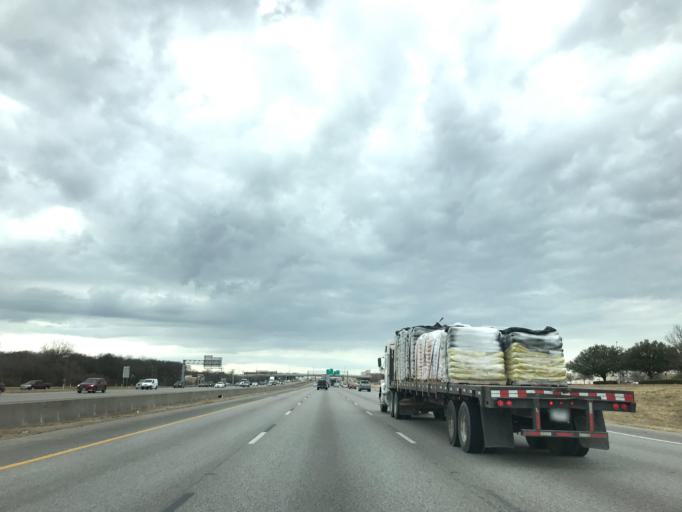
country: US
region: Texas
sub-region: Tarrant County
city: Arlington
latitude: 32.6782
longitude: -97.0962
